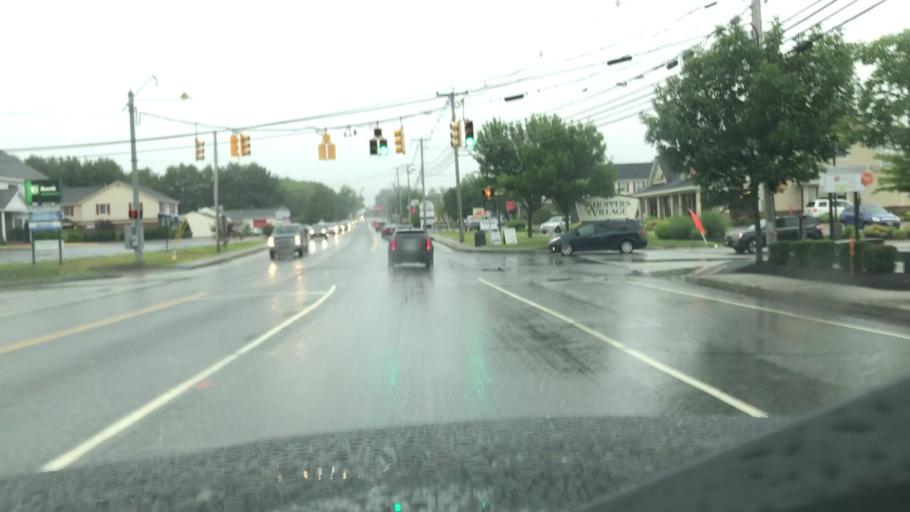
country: US
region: Maine
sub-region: York County
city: Kennebunk
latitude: 43.3942
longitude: -70.5322
